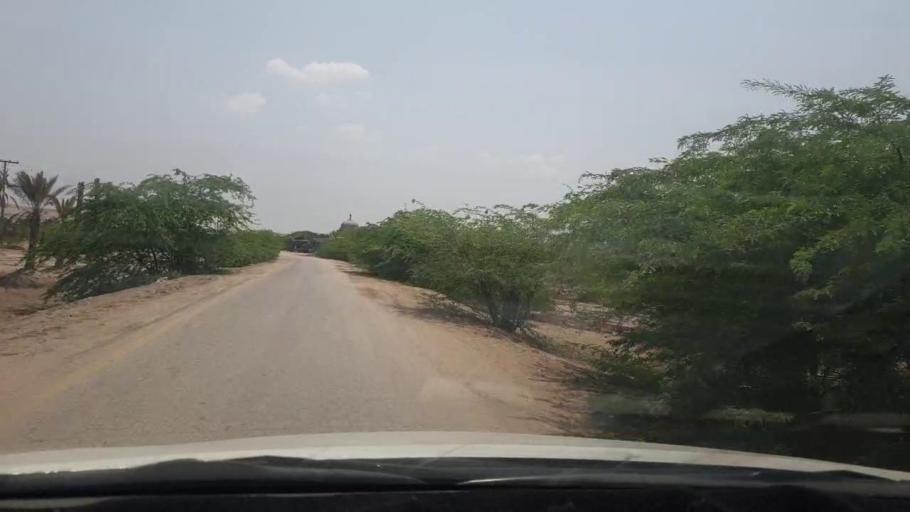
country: PK
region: Sindh
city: Khairpur
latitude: 27.5308
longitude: 68.8993
